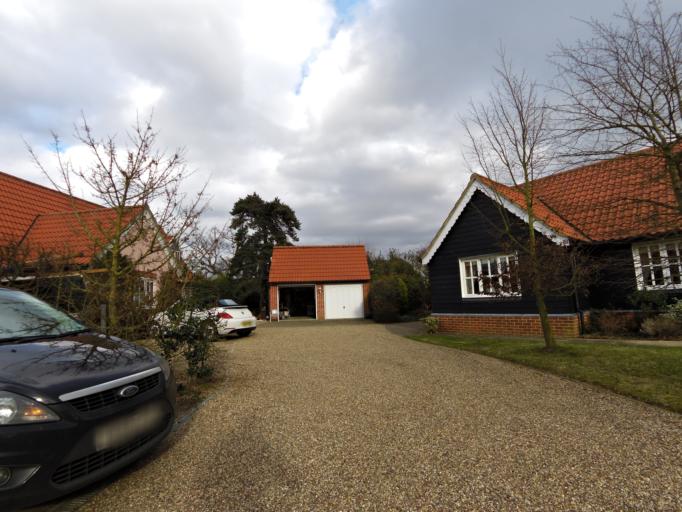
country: GB
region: England
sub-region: Suffolk
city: Woodbridge
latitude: 52.0522
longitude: 1.3232
